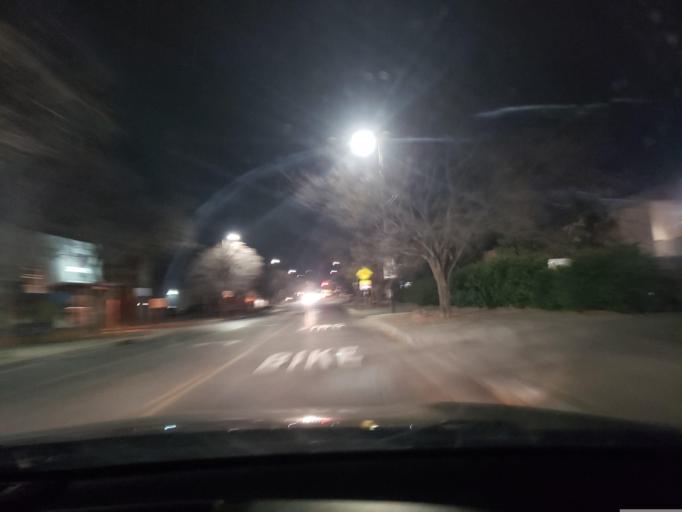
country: US
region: New Mexico
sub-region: Bernalillo County
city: Albuquerque
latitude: 35.0796
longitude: -106.6221
